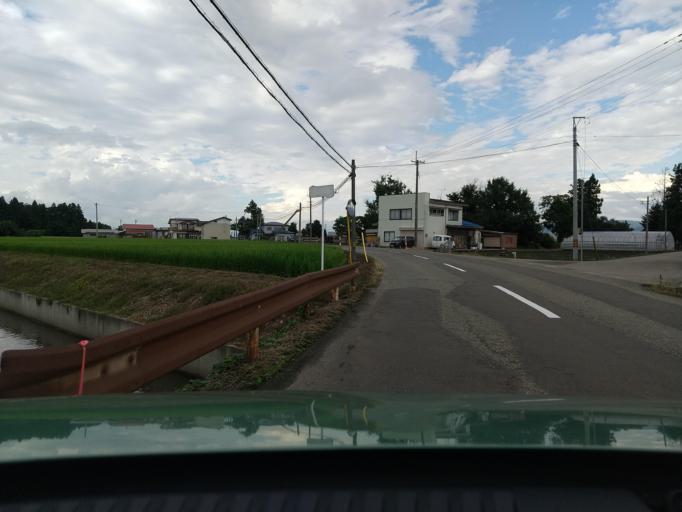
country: JP
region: Akita
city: Yokotemachi
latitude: 39.2912
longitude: 140.4820
